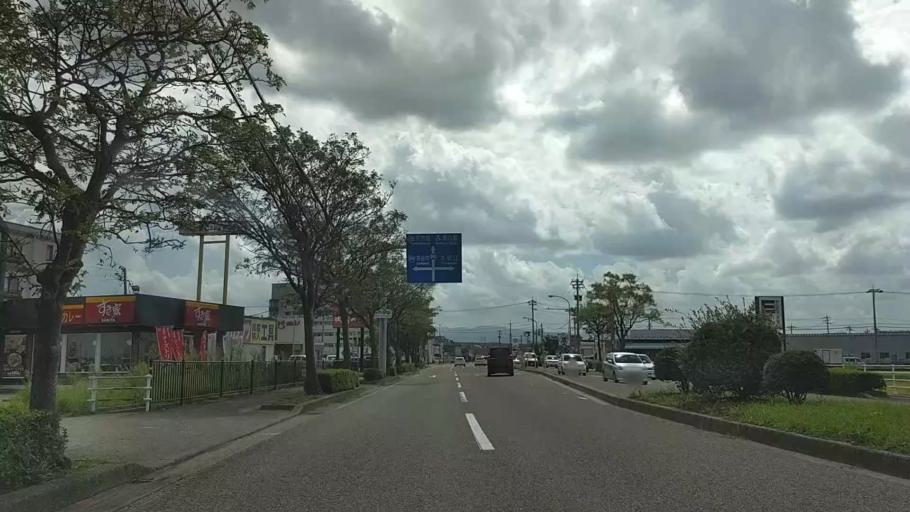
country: JP
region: Ishikawa
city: Kanazawa-shi
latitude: 36.5961
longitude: 136.6625
